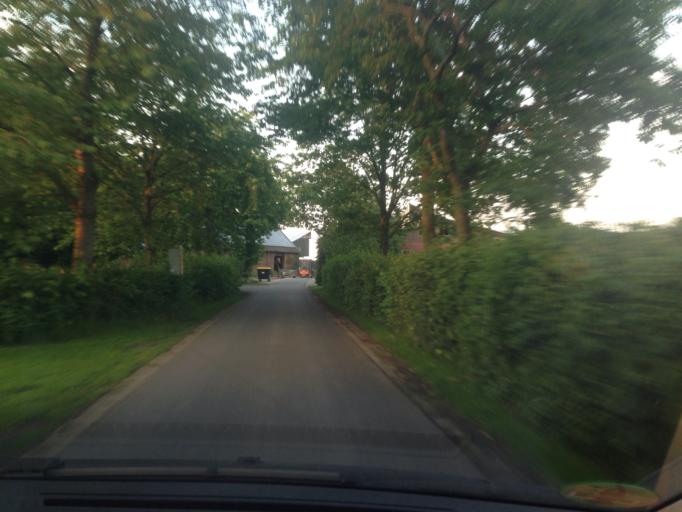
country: DE
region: North Rhine-Westphalia
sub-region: Regierungsbezirk Munster
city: Greven
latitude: 52.0208
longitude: 7.5788
